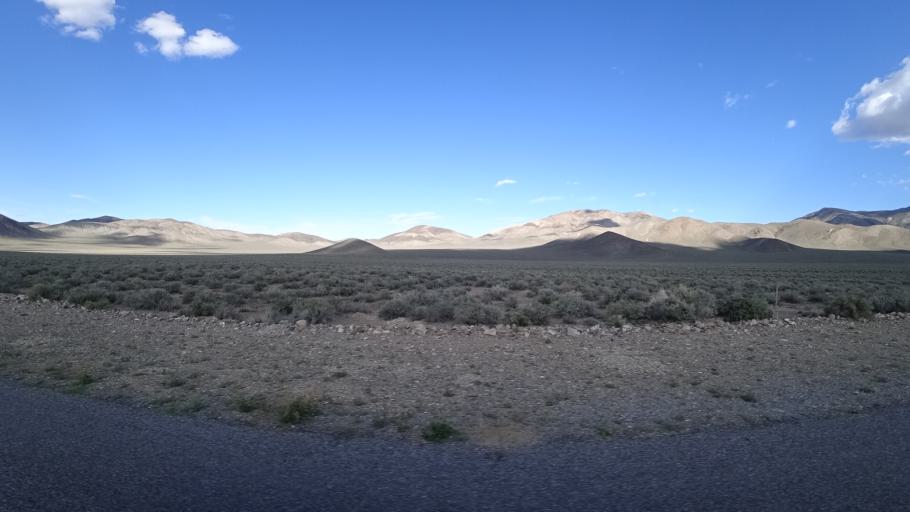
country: US
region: California
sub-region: San Bernardino County
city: Searles Valley
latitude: 36.3581
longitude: -117.1340
